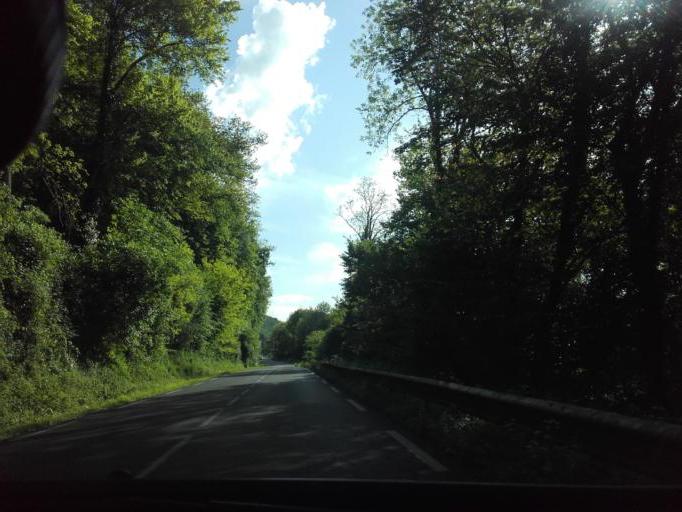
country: FR
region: Aquitaine
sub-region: Departement de la Dordogne
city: Lalinde
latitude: 44.8471
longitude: 0.7970
